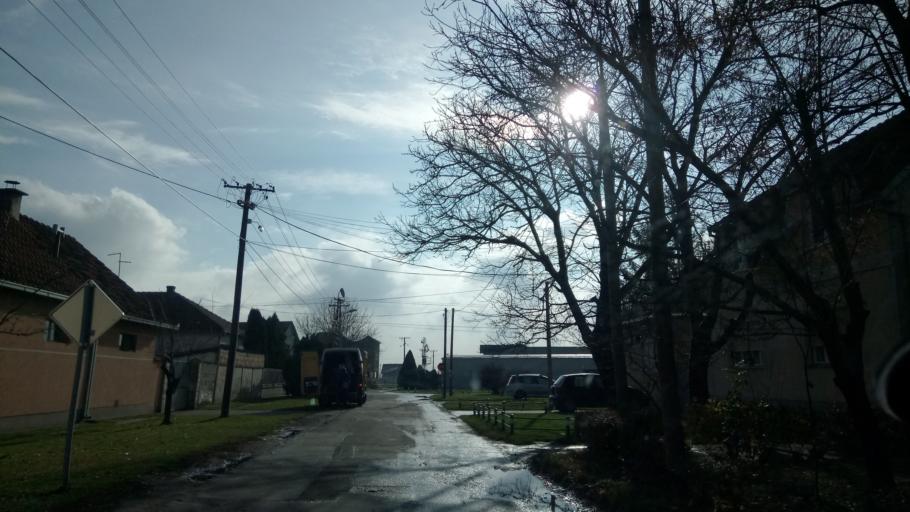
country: RS
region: Autonomna Pokrajina Vojvodina
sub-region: Sremski Okrug
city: Stara Pazova
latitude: 44.9795
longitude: 20.1506
